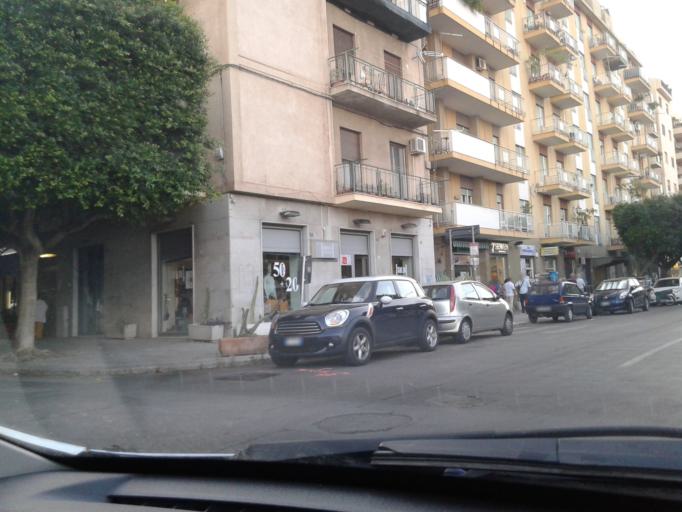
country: IT
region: Sicily
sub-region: Palermo
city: Palermo
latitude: 38.1028
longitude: 13.3365
